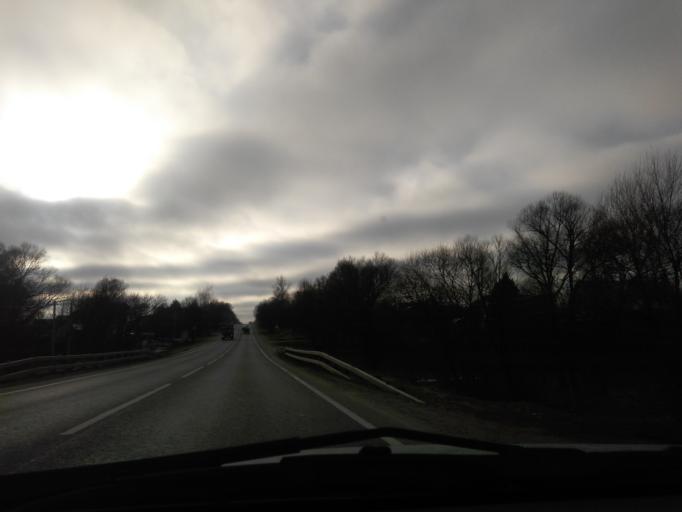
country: RU
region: Moskovskaya
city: Troitsk
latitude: 55.3033
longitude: 37.1413
